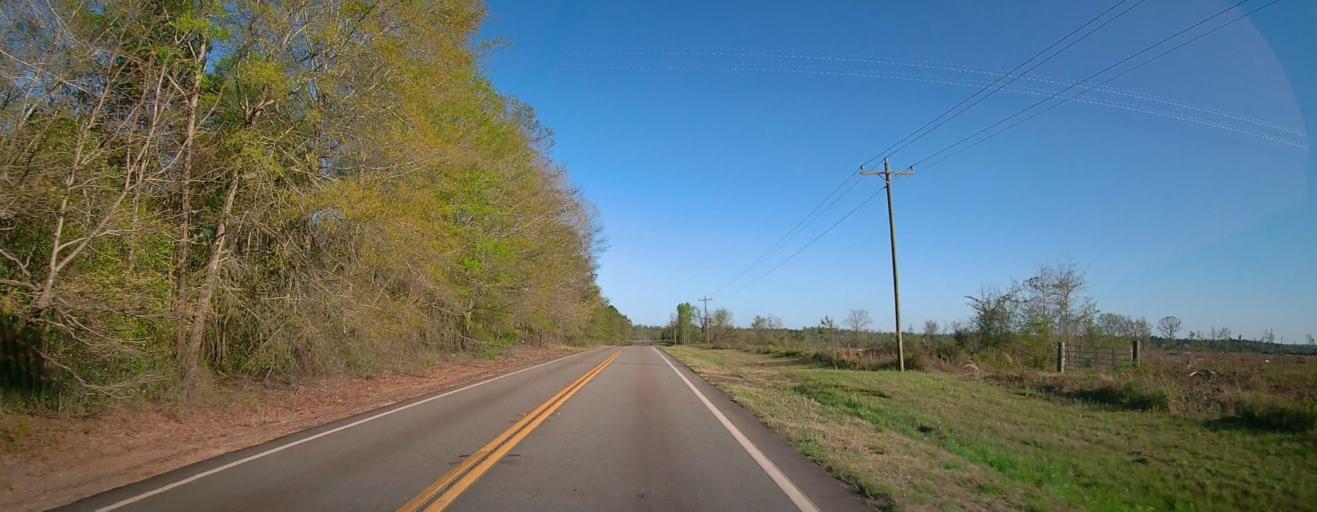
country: US
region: Georgia
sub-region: Wilkinson County
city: Irwinton
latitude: 32.8793
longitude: -83.1264
